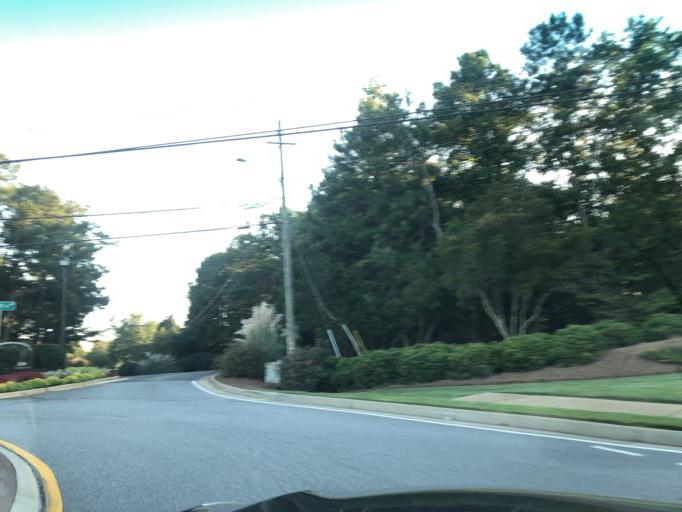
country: US
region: Georgia
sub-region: Muscogee County
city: Columbus
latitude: 32.5520
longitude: -84.8978
